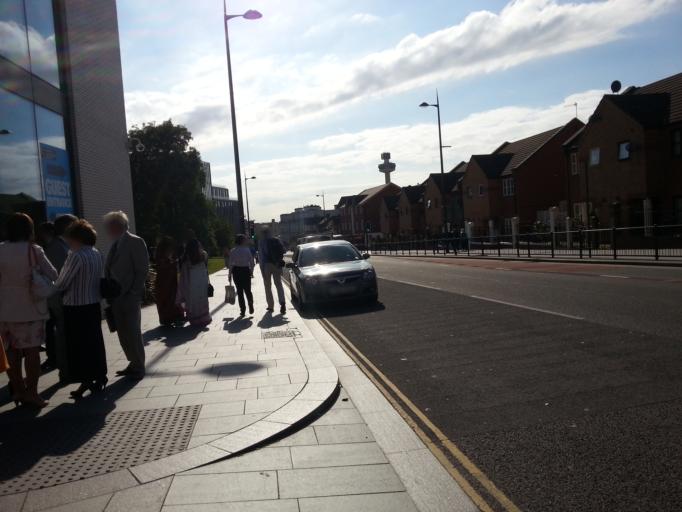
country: GB
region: England
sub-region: Liverpool
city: Liverpool
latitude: 53.4057
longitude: -2.9700
